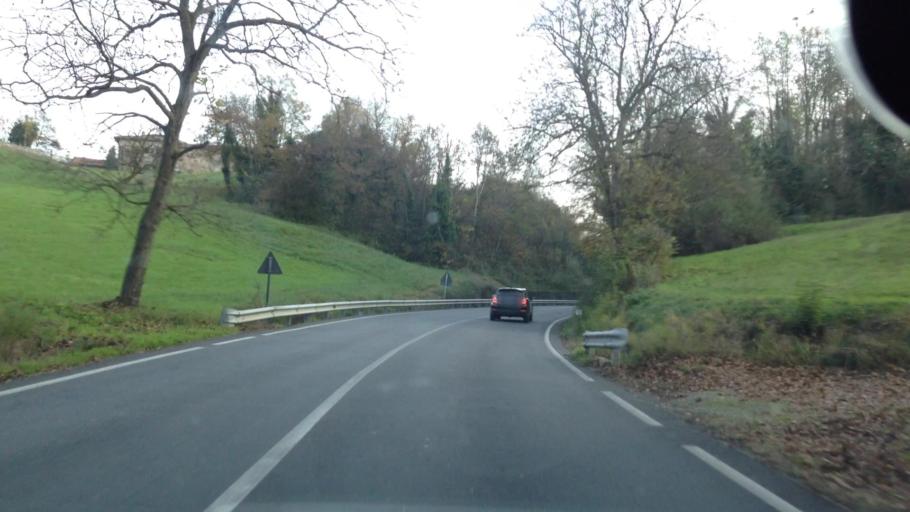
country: IT
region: Piedmont
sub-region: Provincia di Torino
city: Brozolo
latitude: 45.1162
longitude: 8.0661
